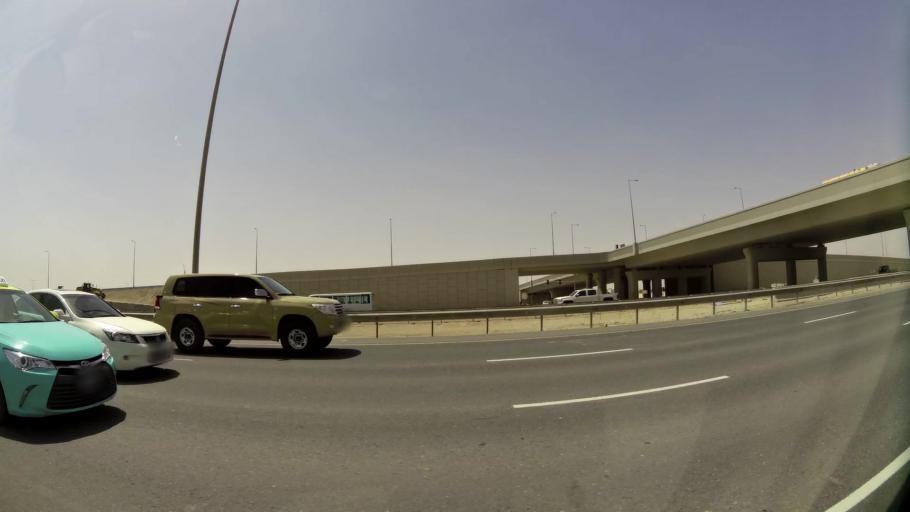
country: QA
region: Baladiyat Umm Salal
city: Umm Salal Muhammad
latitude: 25.4109
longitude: 51.4248
